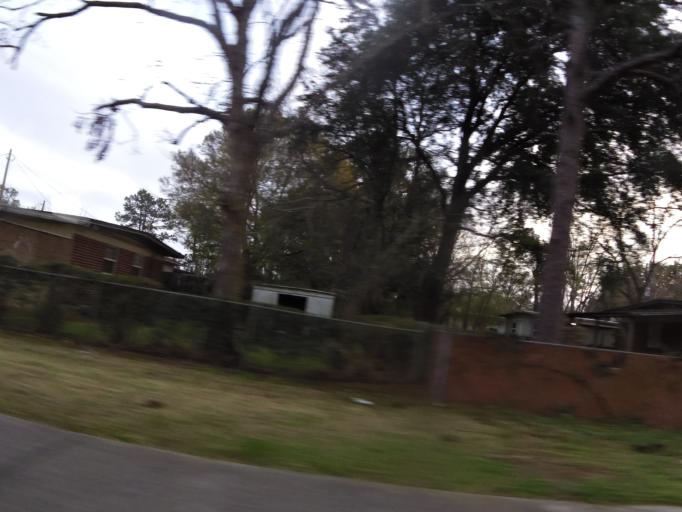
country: US
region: Florida
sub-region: Duval County
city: Jacksonville
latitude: 30.3580
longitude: -81.7003
